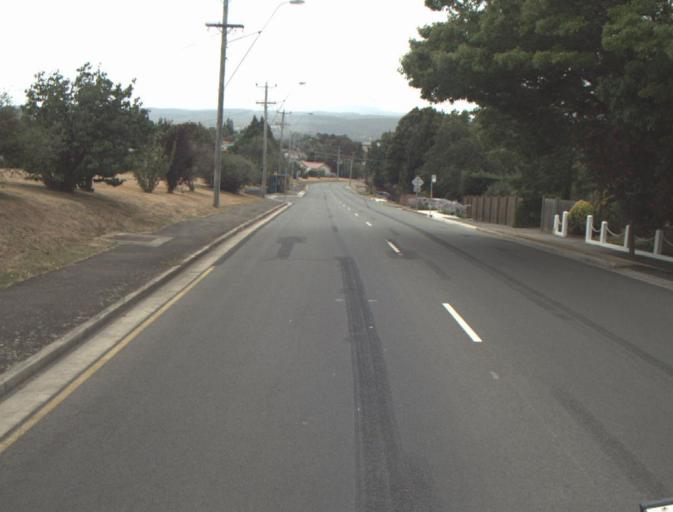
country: AU
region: Tasmania
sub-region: Launceston
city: Summerhill
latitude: -41.4633
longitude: 147.1496
